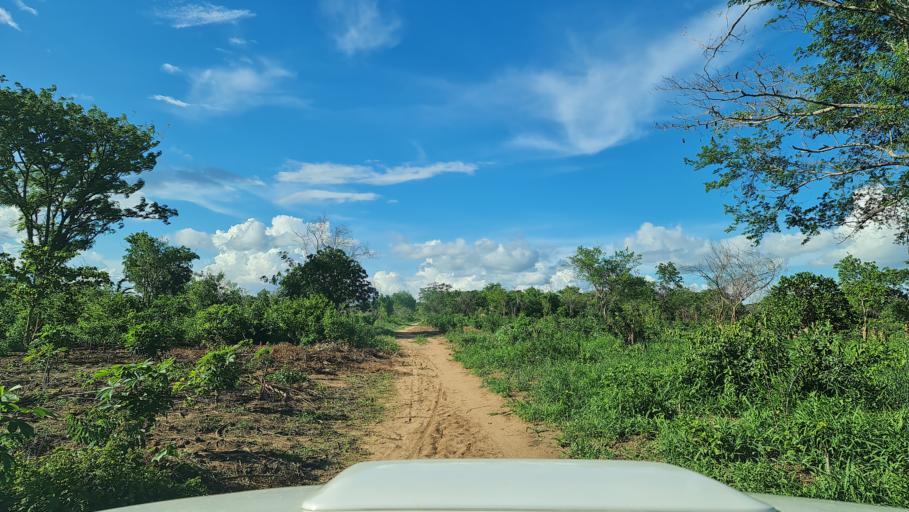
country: MZ
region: Nampula
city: Ilha de Mocambique
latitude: -15.2654
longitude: 40.1860
